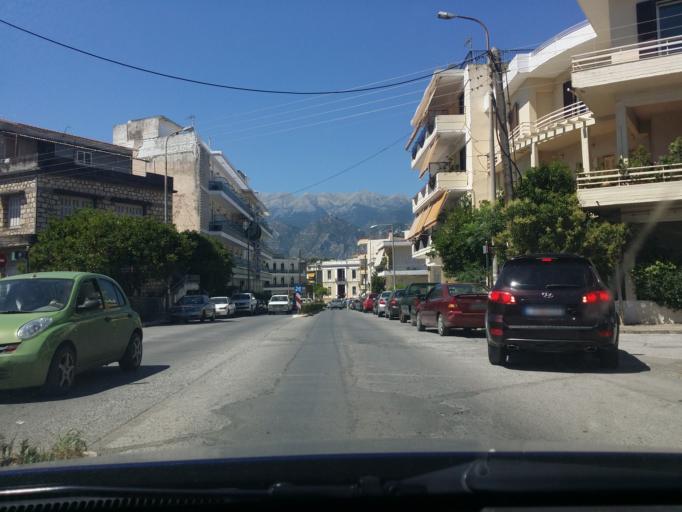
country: GR
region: Peloponnese
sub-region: Nomos Lakonias
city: Sparti
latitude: 37.0777
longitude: 22.4301
